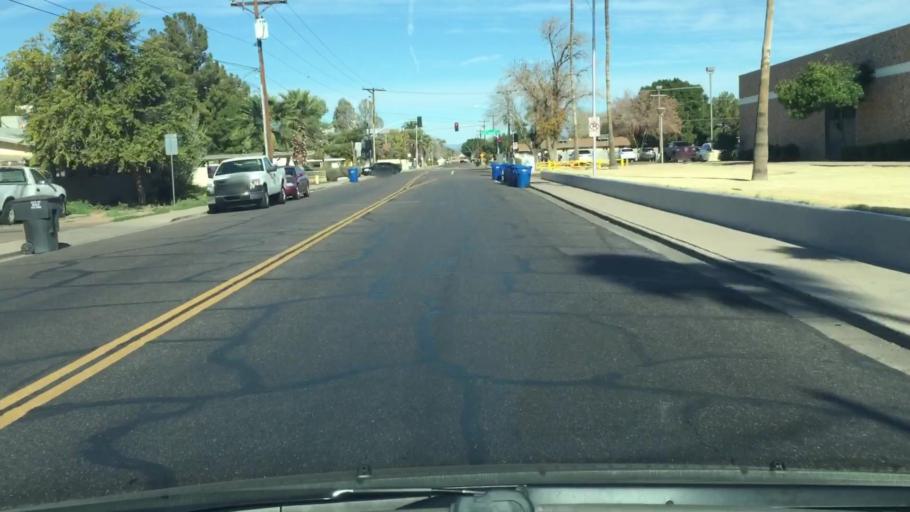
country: US
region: Arizona
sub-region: Maricopa County
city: Mesa
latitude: 33.4284
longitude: -111.8522
